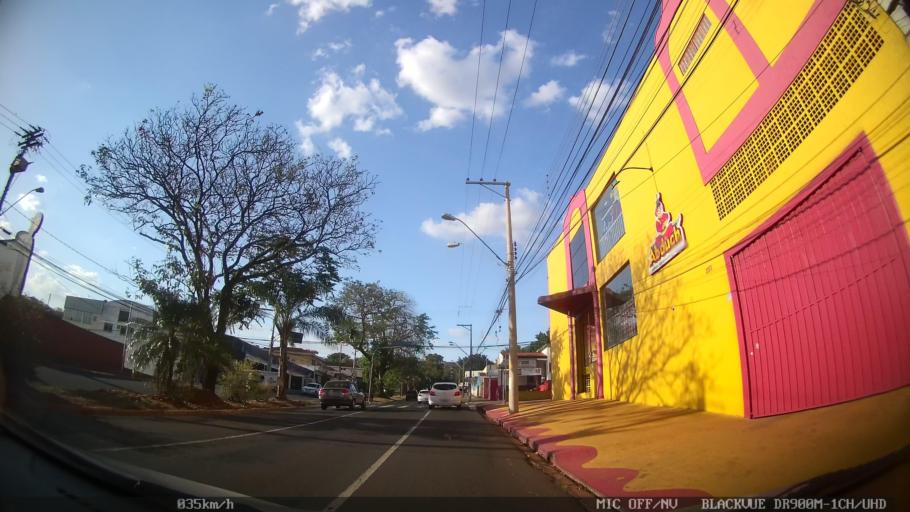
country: BR
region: Sao Paulo
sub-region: Ribeirao Preto
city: Ribeirao Preto
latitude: -21.1780
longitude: -47.7984
